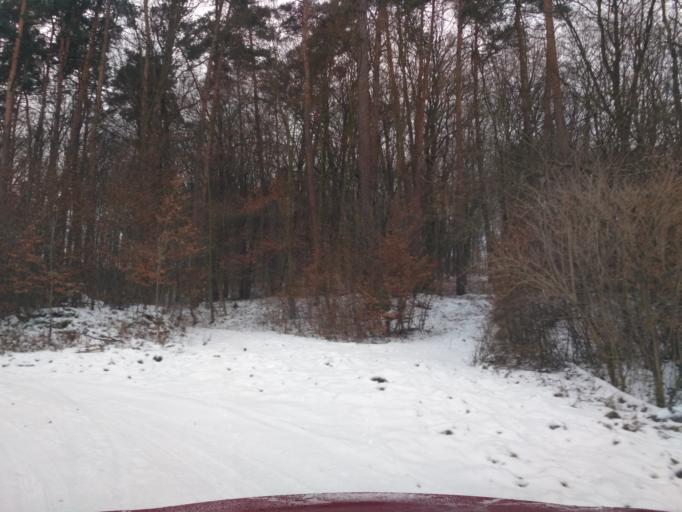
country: SK
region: Presovsky
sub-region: Okres Presov
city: Presov
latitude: 48.9956
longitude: 21.1796
